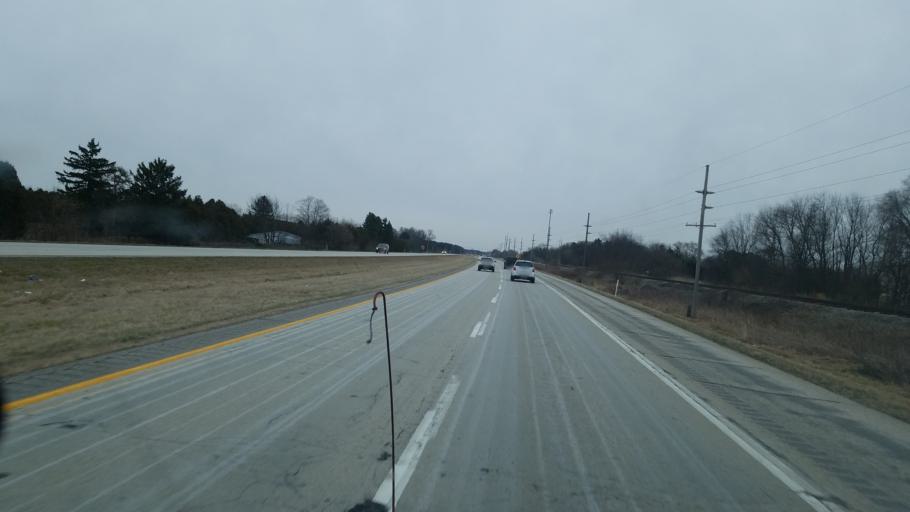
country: US
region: Indiana
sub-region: Starke County
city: Koontz Lake
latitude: 41.3791
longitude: -86.5588
